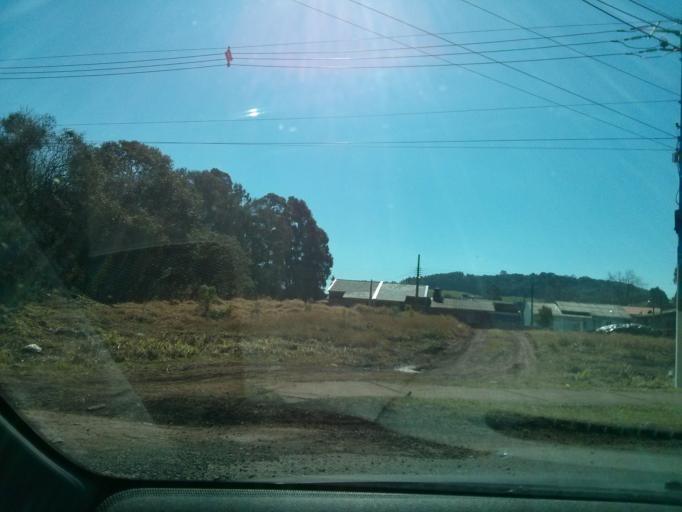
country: BR
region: Santa Catarina
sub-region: Chapeco
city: Chapeco
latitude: -27.0901
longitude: -52.6833
